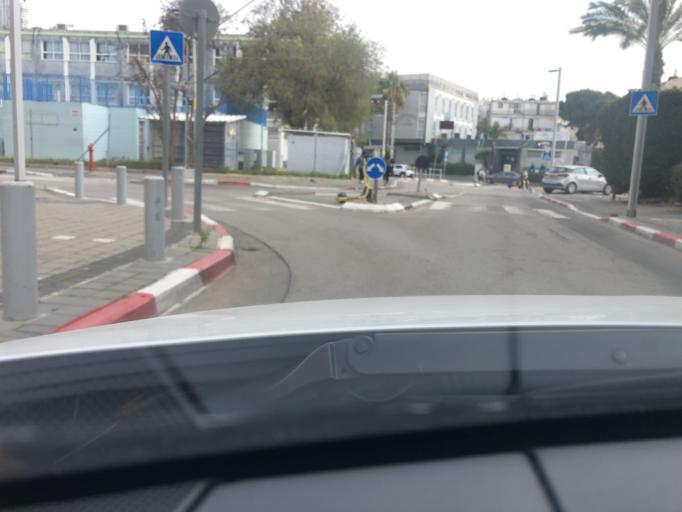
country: IL
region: Tel Aviv
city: Bat Yam
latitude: 32.0195
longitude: 34.7466
